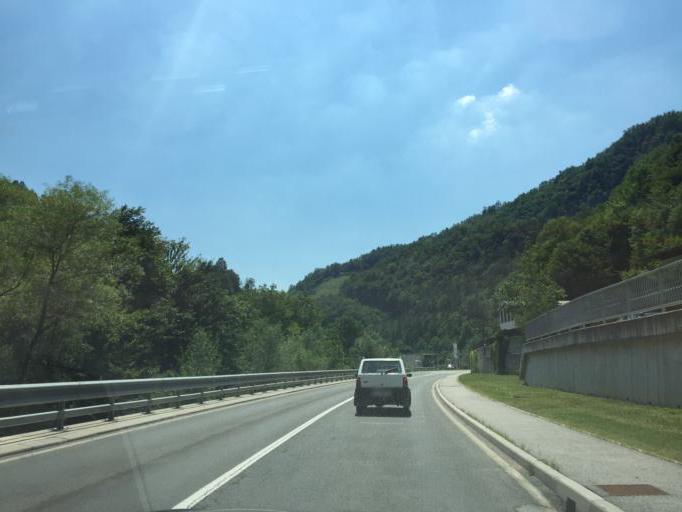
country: SI
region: Idrija
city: Spodnja Idrija
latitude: 46.0183
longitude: 14.0297
